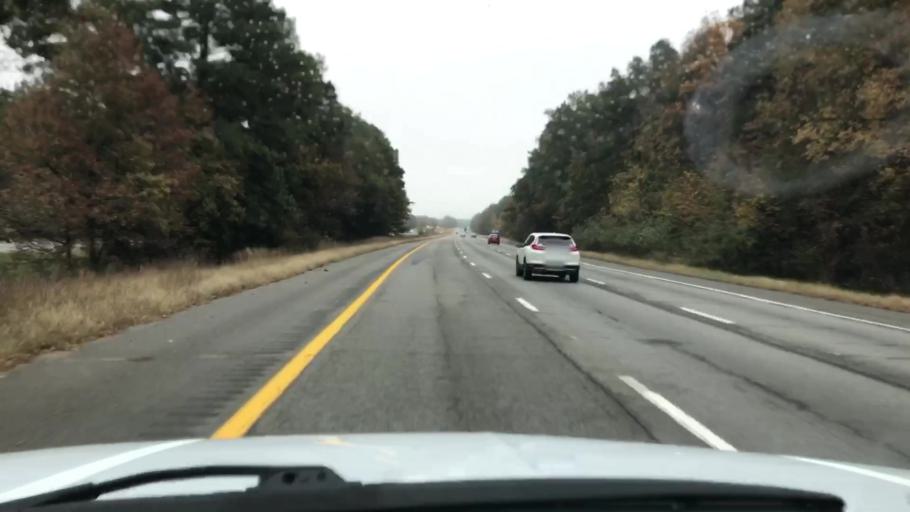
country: US
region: Virginia
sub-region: Henrico County
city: Glen Allen
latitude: 37.6802
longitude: -77.5156
